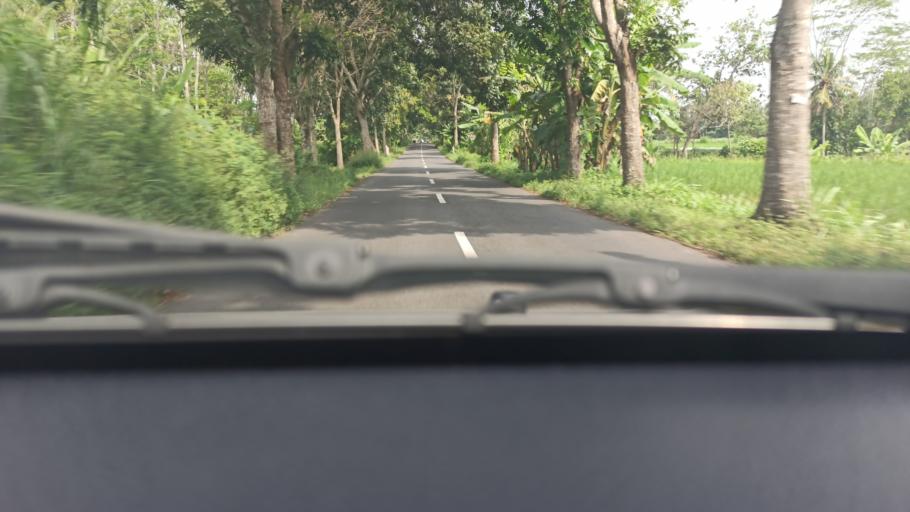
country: ID
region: Daerah Istimewa Yogyakarta
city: Sleman
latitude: -7.6979
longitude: 110.2985
